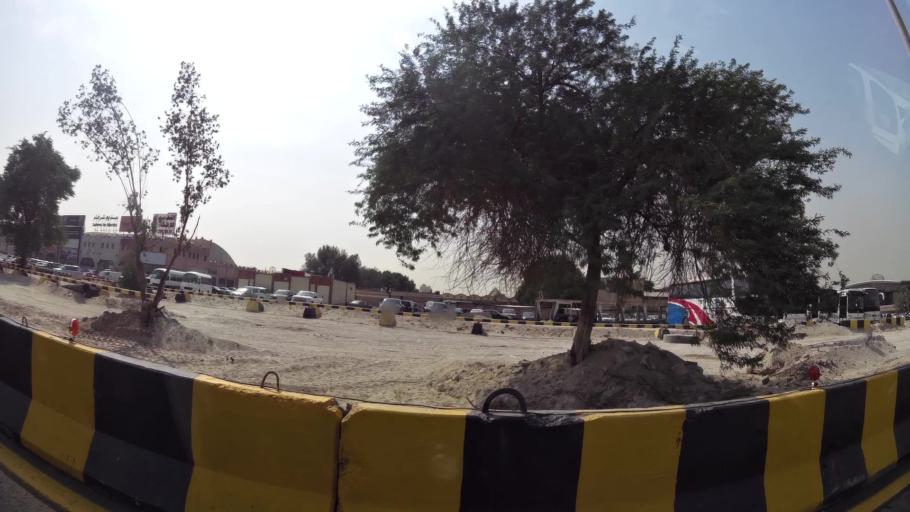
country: KW
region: Al Asimah
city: Ash Shamiyah
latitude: 29.3351
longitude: 47.9502
